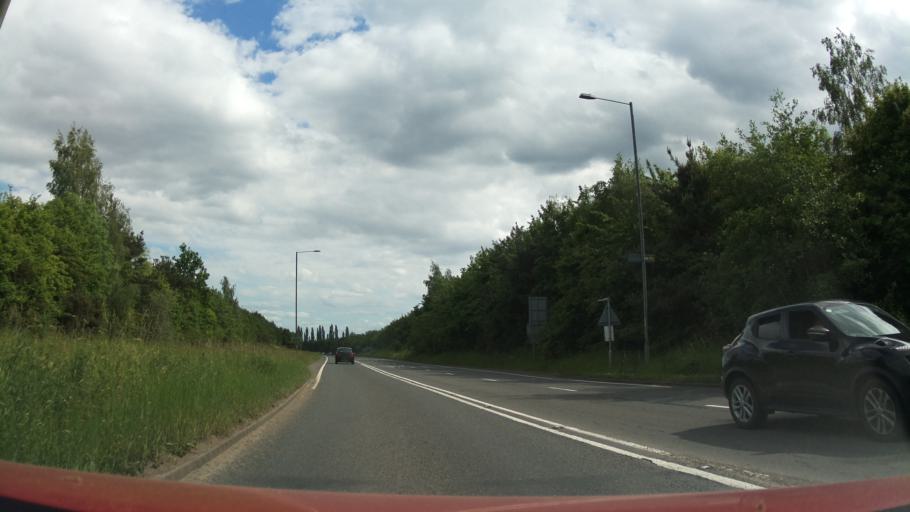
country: GB
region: England
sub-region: Worcestershire
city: Bransford
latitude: 52.1882
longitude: -2.2653
